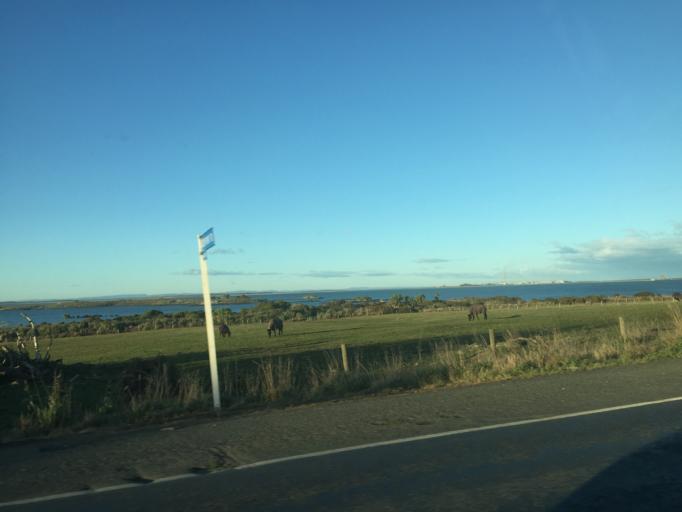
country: NZ
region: Southland
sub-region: Invercargill City
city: Bluff
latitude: -46.5759
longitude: 168.3032
